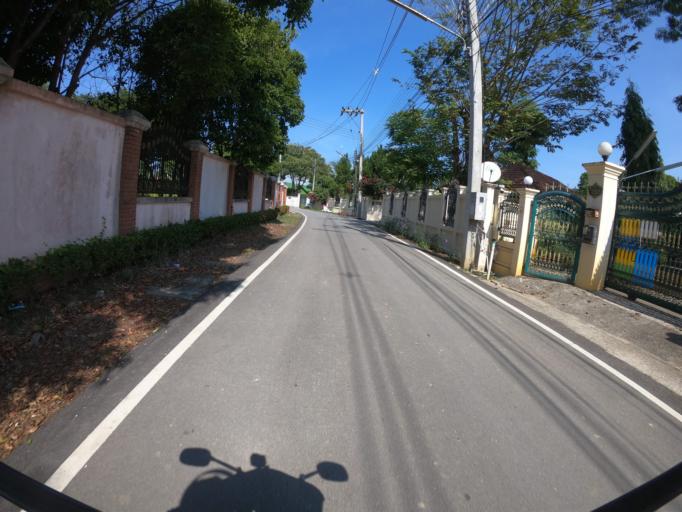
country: TH
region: Chiang Mai
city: San Sai
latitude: 18.8578
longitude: 98.9938
